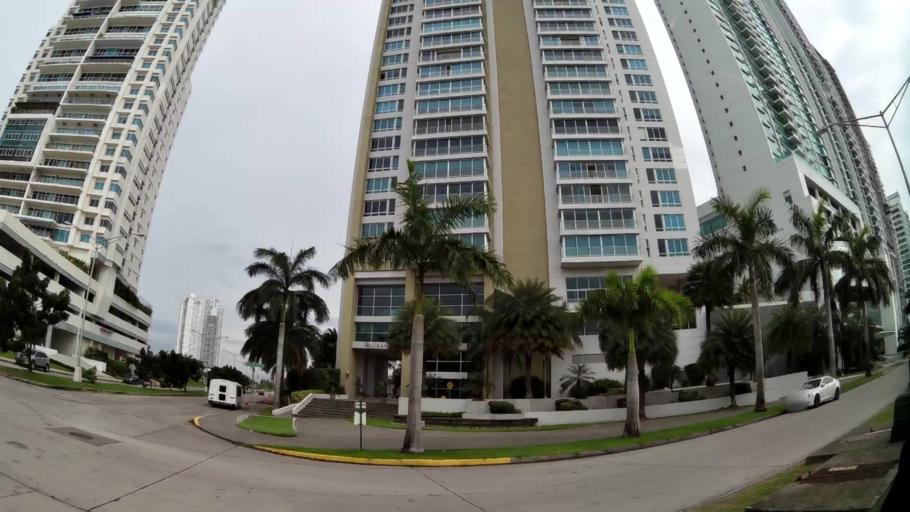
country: PA
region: Panama
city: San Miguelito
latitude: 9.0100
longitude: -79.4649
